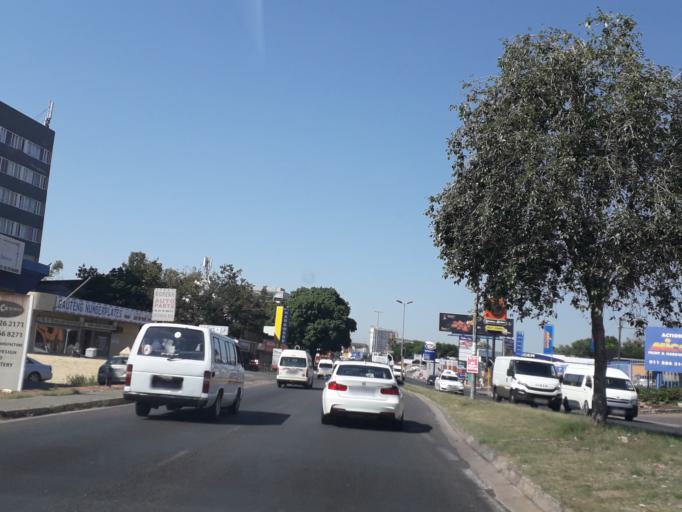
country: ZA
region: Gauteng
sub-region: City of Johannesburg Metropolitan Municipality
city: Johannesburg
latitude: -26.0809
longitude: 28.0095
